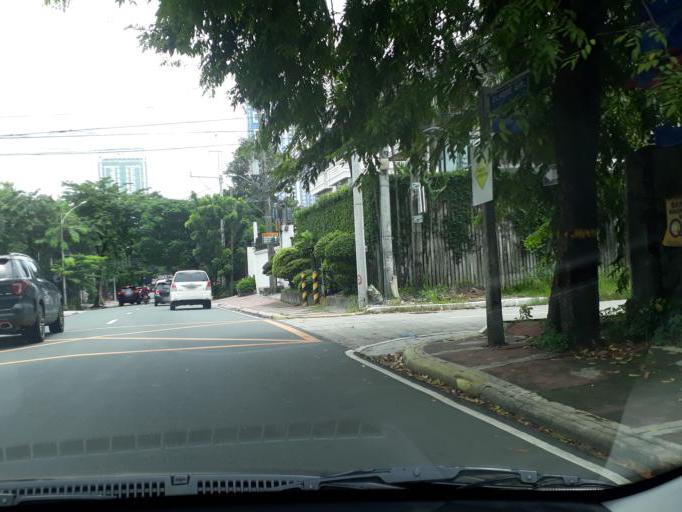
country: PH
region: Metro Manila
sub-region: San Juan
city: San Juan
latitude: 14.6178
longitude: 121.0322
